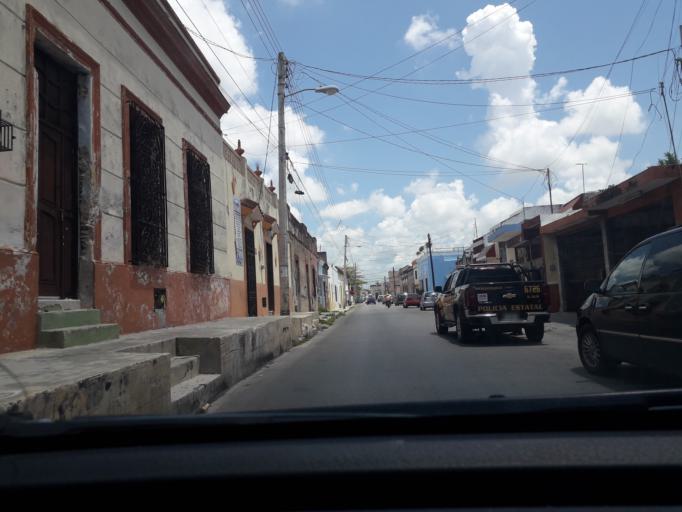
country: MX
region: Yucatan
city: Merida
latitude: 20.9570
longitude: -89.6201
